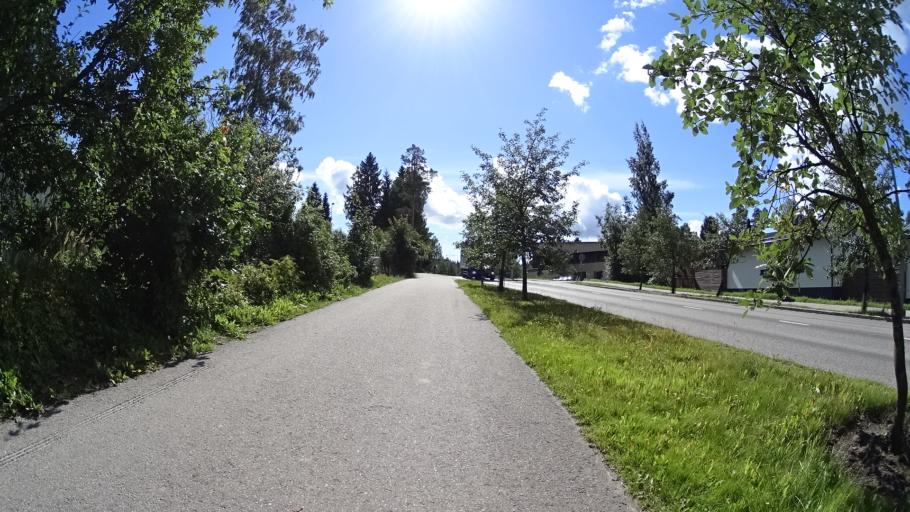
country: FI
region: Uusimaa
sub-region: Helsinki
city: Kauniainen
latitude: 60.2361
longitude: 24.7437
